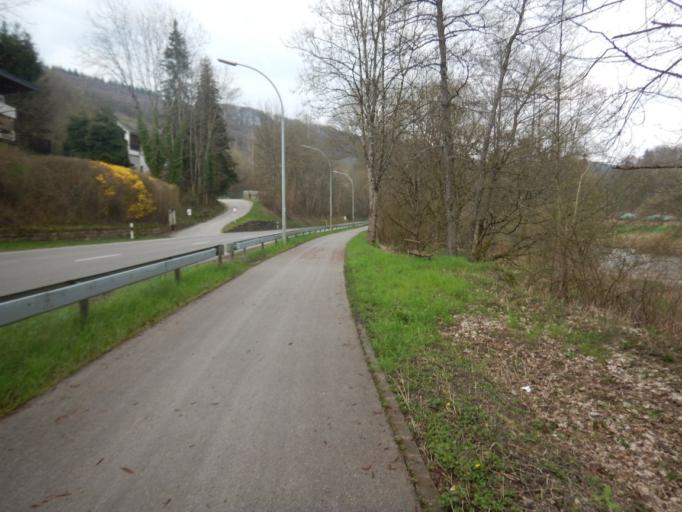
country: LU
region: Grevenmacher
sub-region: Canton d'Echternach
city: Berdorf
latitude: 49.8360
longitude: 6.3262
